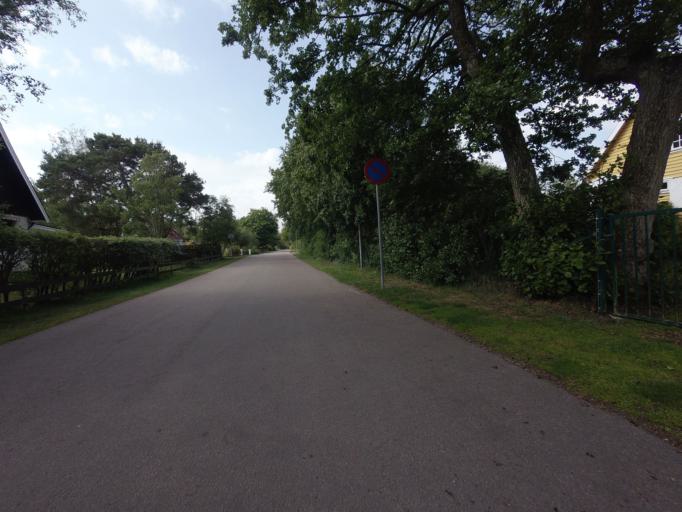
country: SE
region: Skane
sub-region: Angelholms Kommun
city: AEngelholm
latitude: 56.2572
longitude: 12.8351
